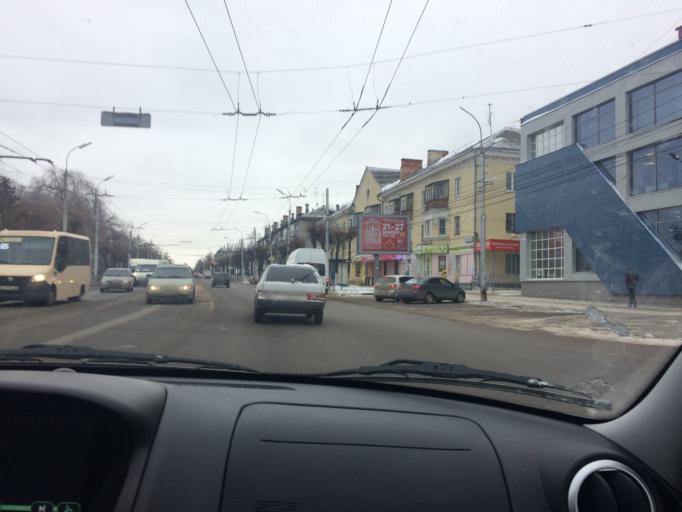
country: RU
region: Rjazan
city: Ryazan'
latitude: 54.6250
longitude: 39.7167
